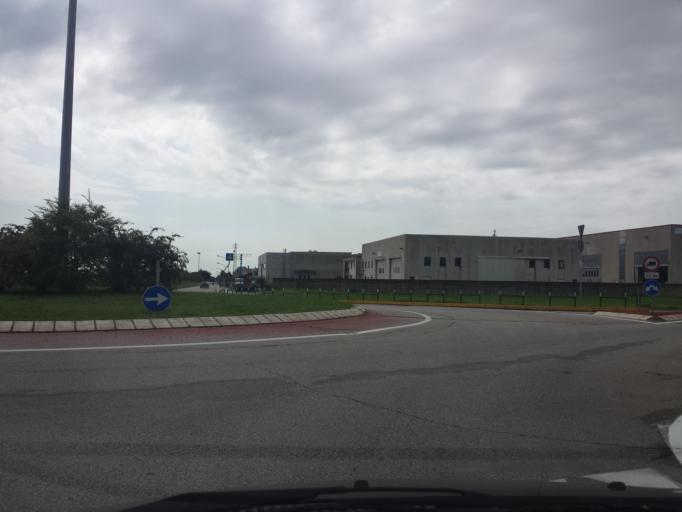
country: IT
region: Veneto
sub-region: Provincia di Padova
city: Galliera Veneta
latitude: 45.6719
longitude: 11.8168
